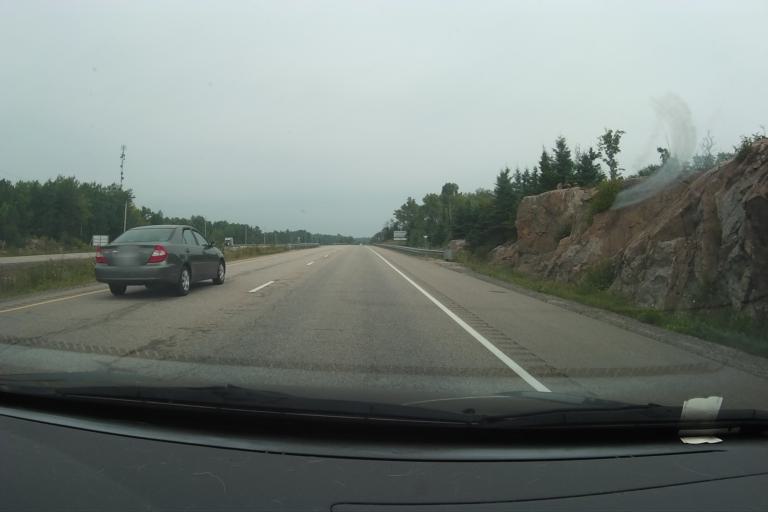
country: CA
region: Ontario
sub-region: Nipissing District
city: North Bay
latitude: 46.2208
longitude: -79.3500
